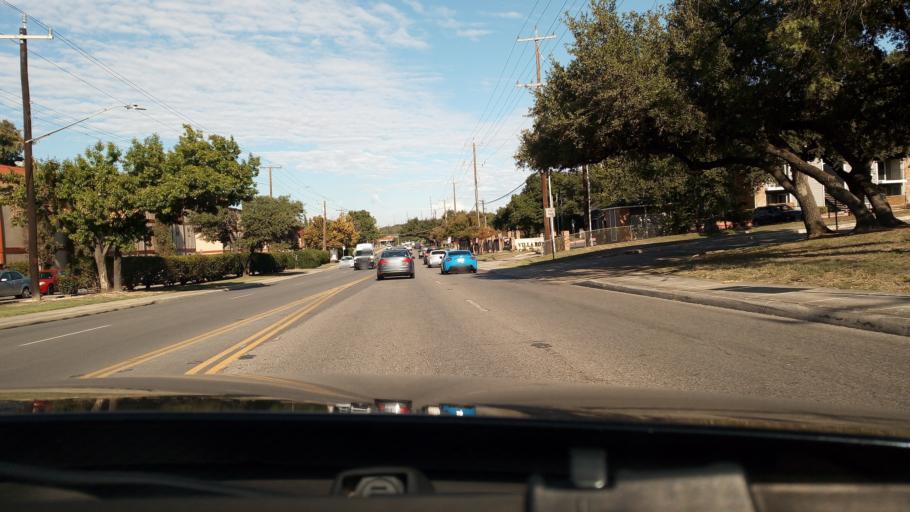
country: US
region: Texas
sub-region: Bexar County
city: Alamo Heights
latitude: 29.5274
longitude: -98.4362
